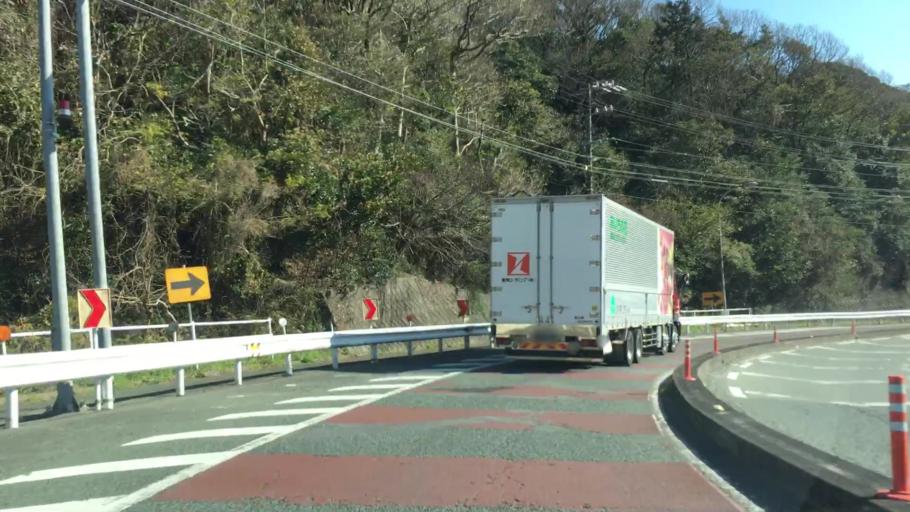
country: JP
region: Shizuoka
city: Kosai-shi
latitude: 34.6831
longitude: 137.5084
